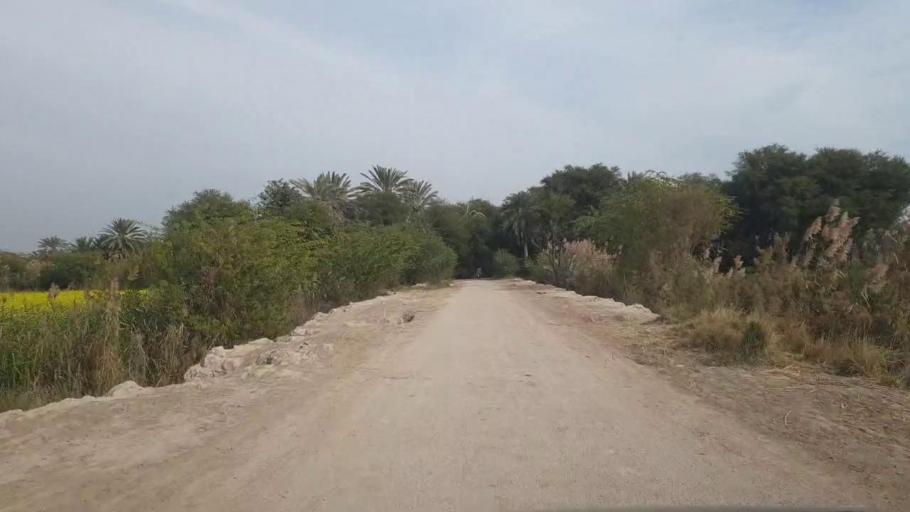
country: PK
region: Sindh
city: Shahpur Chakar
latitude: 26.0797
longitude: 68.4970
